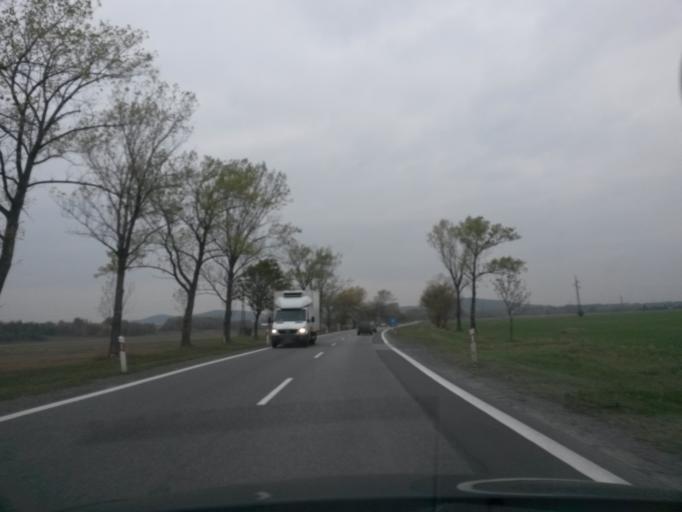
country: PL
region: Lower Silesian Voivodeship
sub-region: Powiat zabkowicki
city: Bardo
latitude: 50.5135
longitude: 16.7596
